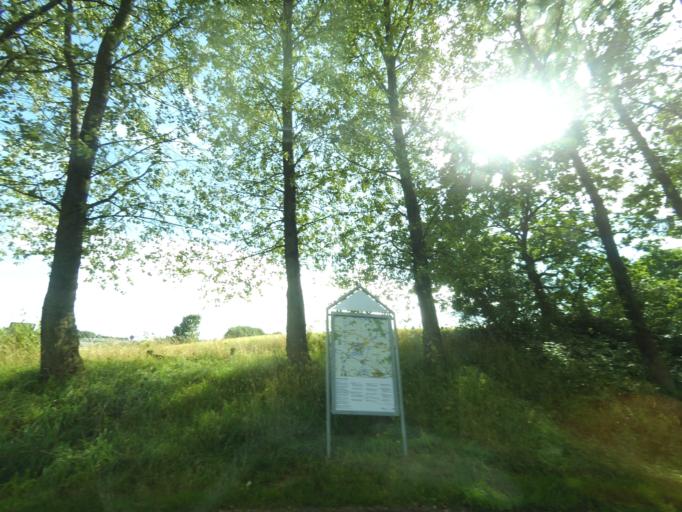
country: DK
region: South Denmark
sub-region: Assens Kommune
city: Vissenbjerg
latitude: 55.4003
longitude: 10.1542
